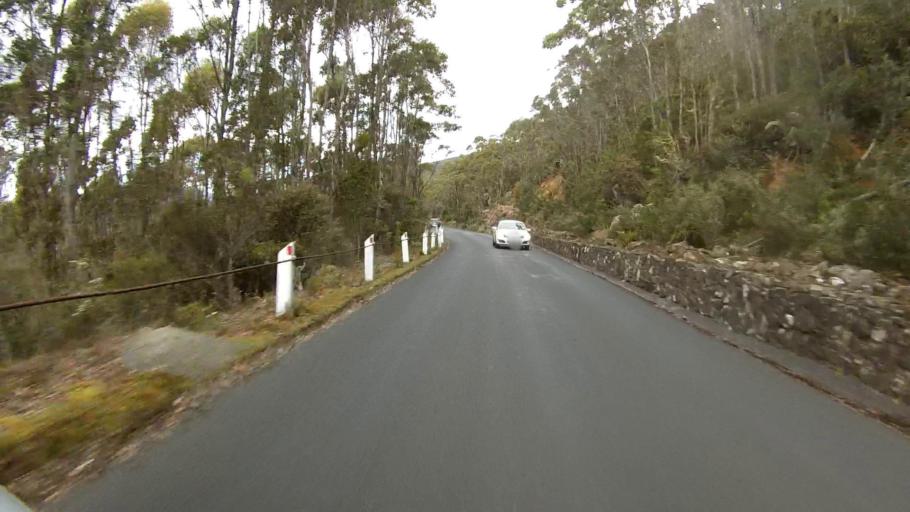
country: AU
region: Tasmania
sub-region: Glenorchy
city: West Moonah
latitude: -42.8972
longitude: 147.2441
